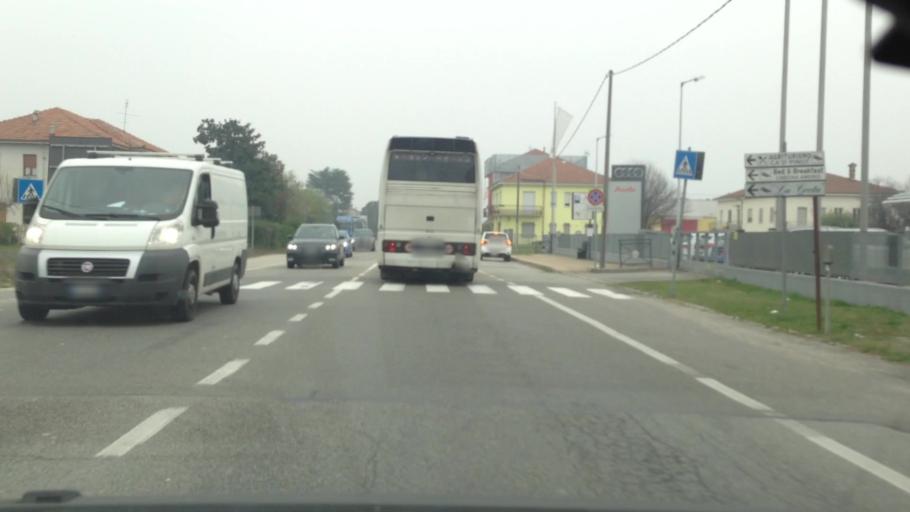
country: IT
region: Piedmont
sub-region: Provincia di Asti
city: Azzano d'Asti
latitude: 44.9065
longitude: 8.2569
